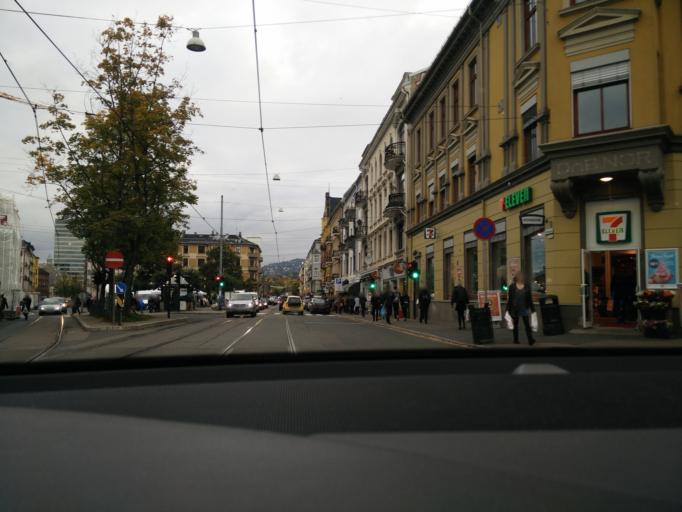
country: NO
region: Oslo
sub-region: Oslo
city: Oslo
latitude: 59.9279
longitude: 10.7192
